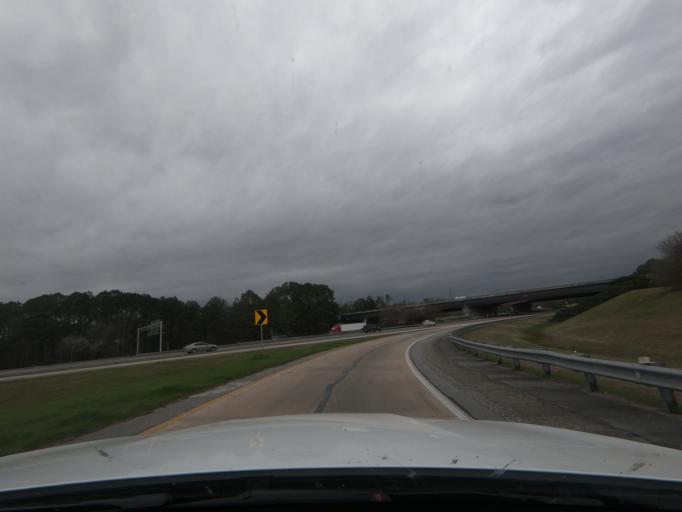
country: US
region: Alabama
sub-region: Russell County
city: Phenix City
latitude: 32.5435
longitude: -84.9599
